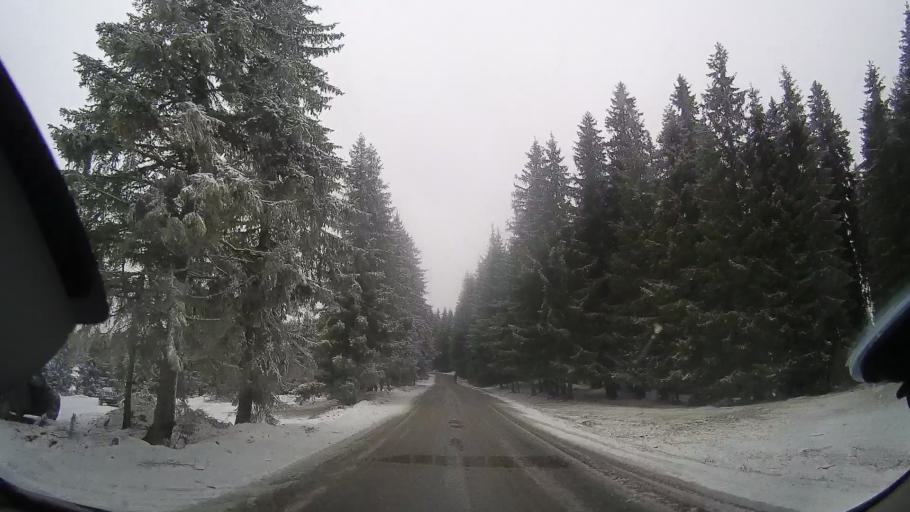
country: RO
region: Cluj
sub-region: Comuna Belis
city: Belis
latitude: 46.6385
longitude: 23.0521
